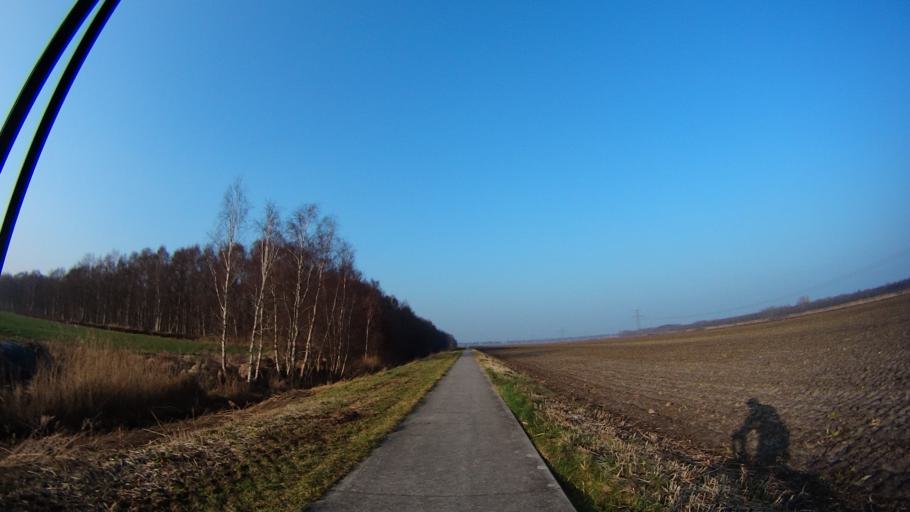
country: NL
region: Drenthe
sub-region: Gemeente Emmen
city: Emmen
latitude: 52.7863
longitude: 6.9670
